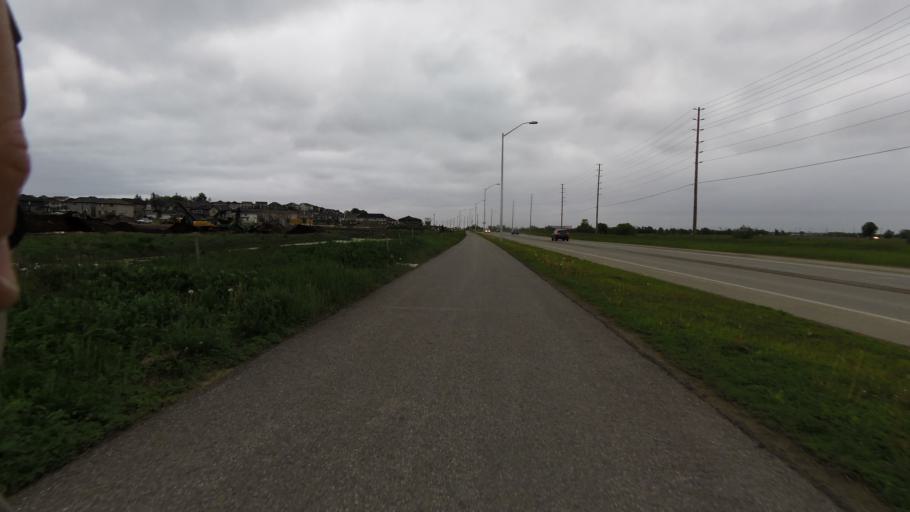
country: CA
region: Ontario
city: Bells Corners
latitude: 45.3194
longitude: -75.9466
